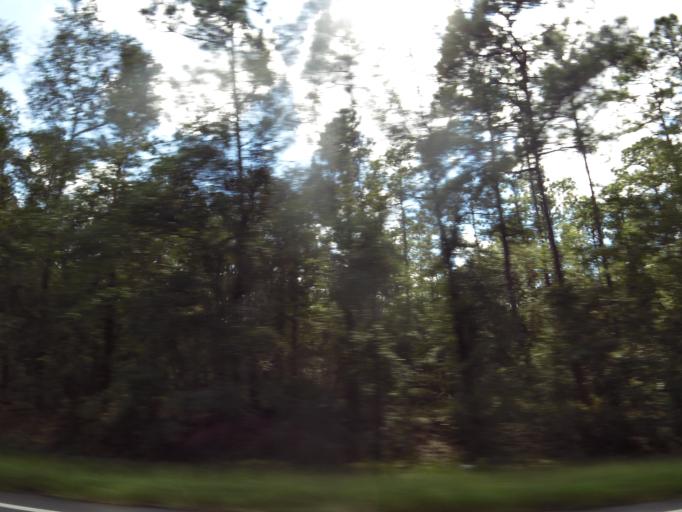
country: US
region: Georgia
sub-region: Echols County
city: Statenville
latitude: 30.7260
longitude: -83.0787
